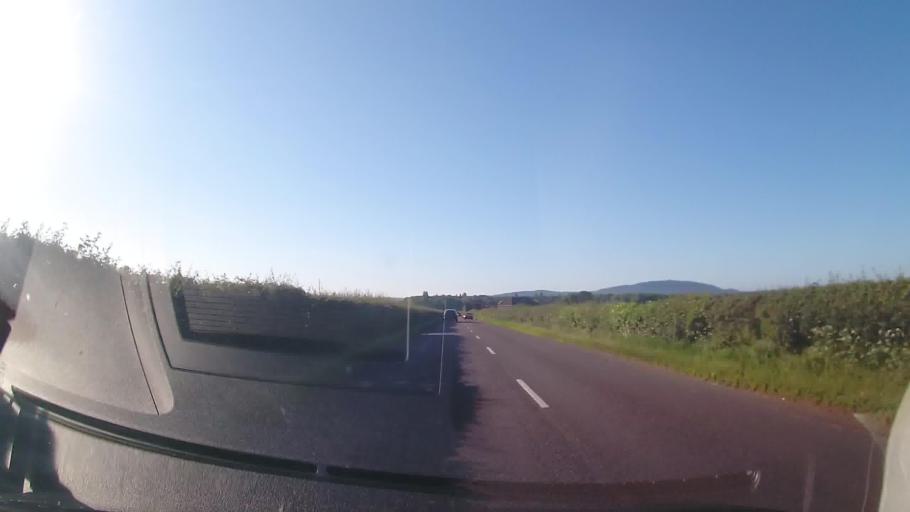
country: GB
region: England
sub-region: Shropshire
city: Withington
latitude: 52.7471
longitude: -2.5857
